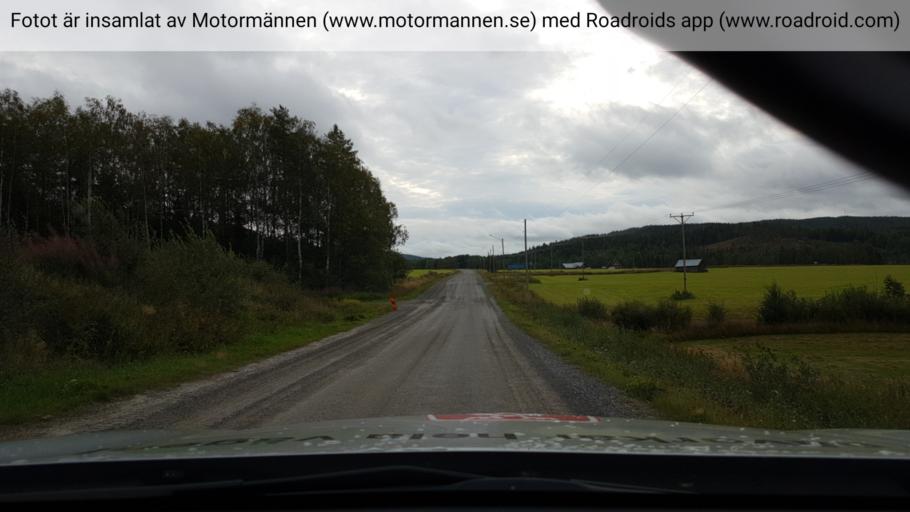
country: SE
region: Vaesterbotten
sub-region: Vannas Kommun
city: Vannasby
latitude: 64.1036
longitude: 19.9820
